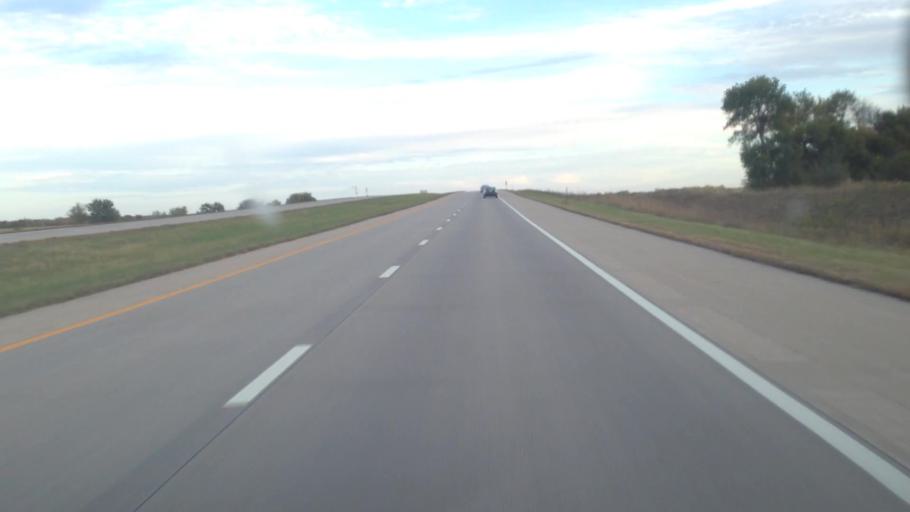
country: US
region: Kansas
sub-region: Franklin County
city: Ottawa
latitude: 38.6571
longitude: -95.2403
